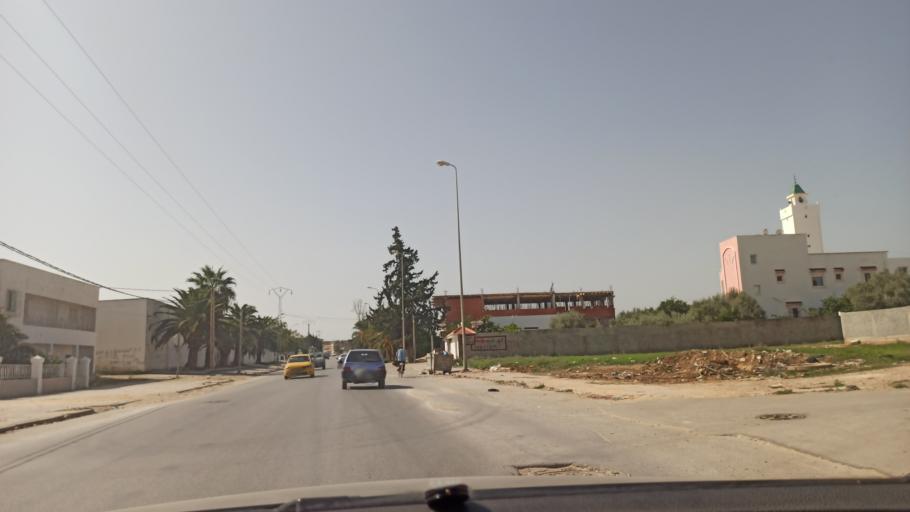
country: TN
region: Manouba
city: Manouba
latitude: 36.7601
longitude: 10.1065
